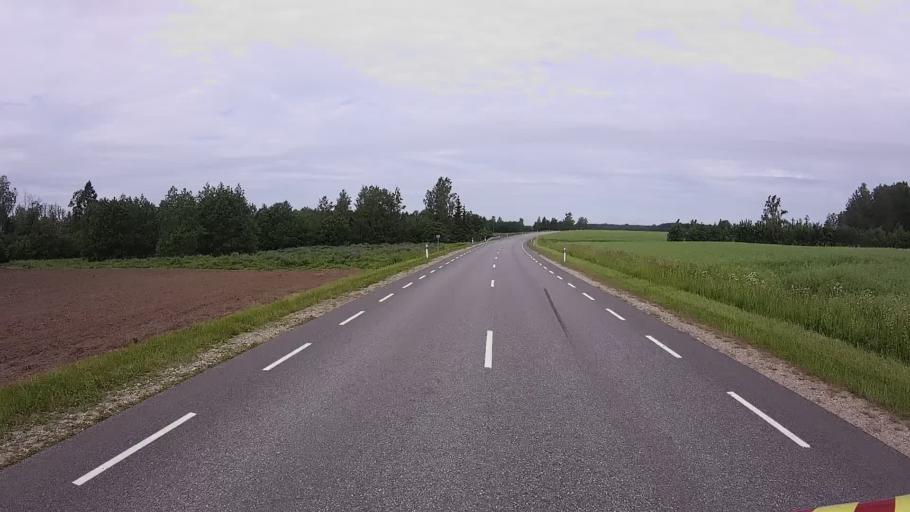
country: EE
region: Viljandimaa
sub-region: Karksi vald
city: Karksi-Nuia
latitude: 58.1600
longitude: 25.5907
